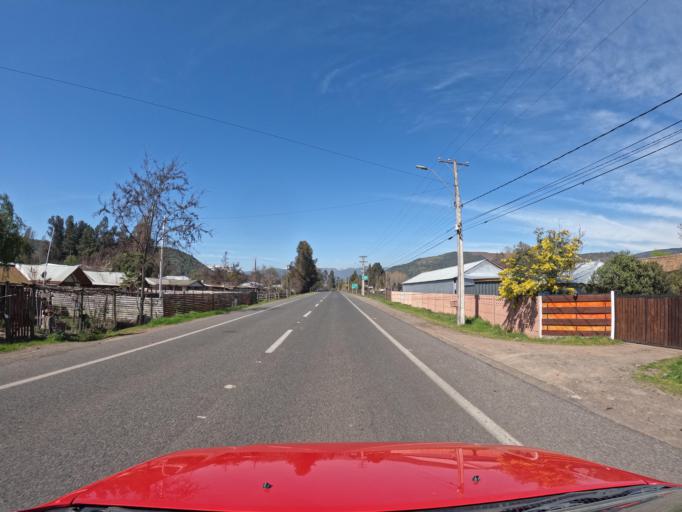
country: CL
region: Maule
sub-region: Provincia de Curico
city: Teno
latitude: -34.9775
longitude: -70.9949
